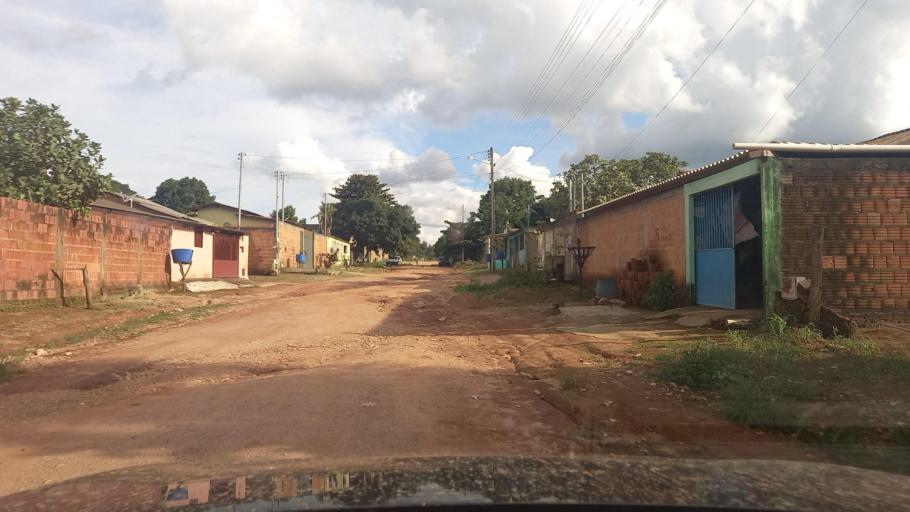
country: BR
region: Goias
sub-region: Cavalcante
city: Cavalcante
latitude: -13.7967
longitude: -47.4436
